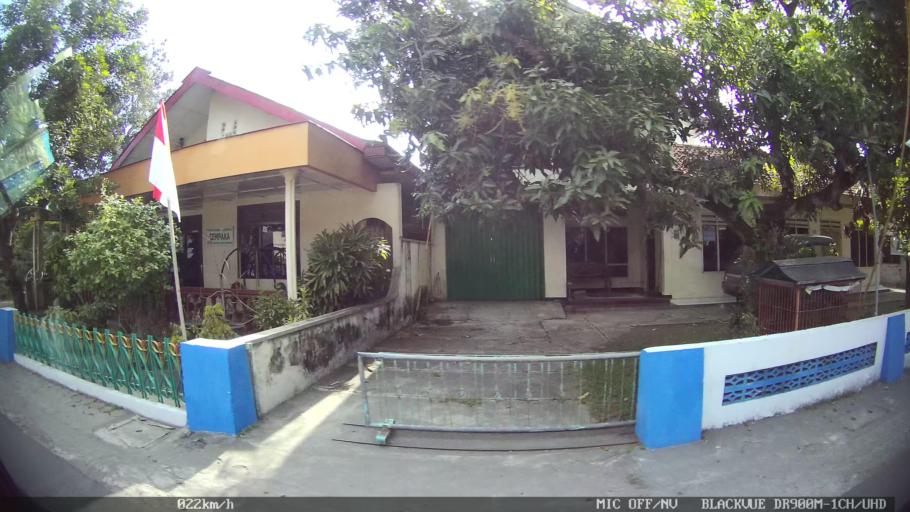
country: ID
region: Daerah Istimewa Yogyakarta
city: Gamping Lor
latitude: -7.7943
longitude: 110.3439
